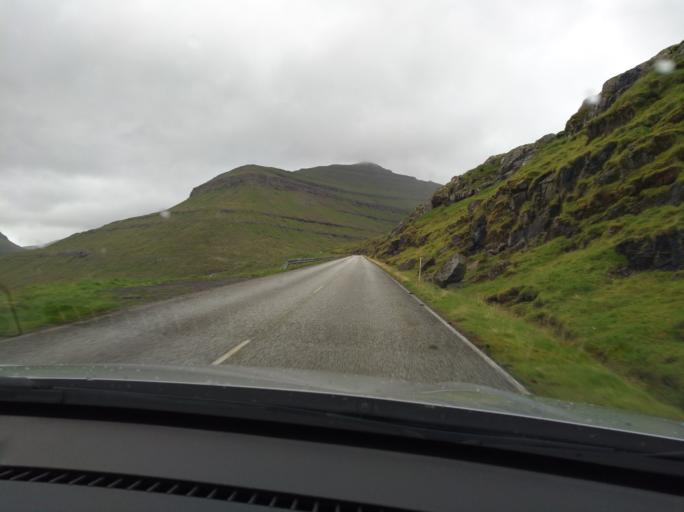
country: FO
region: Eysturoy
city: Fuglafjordur
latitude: 62.2190
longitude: -6.8678
